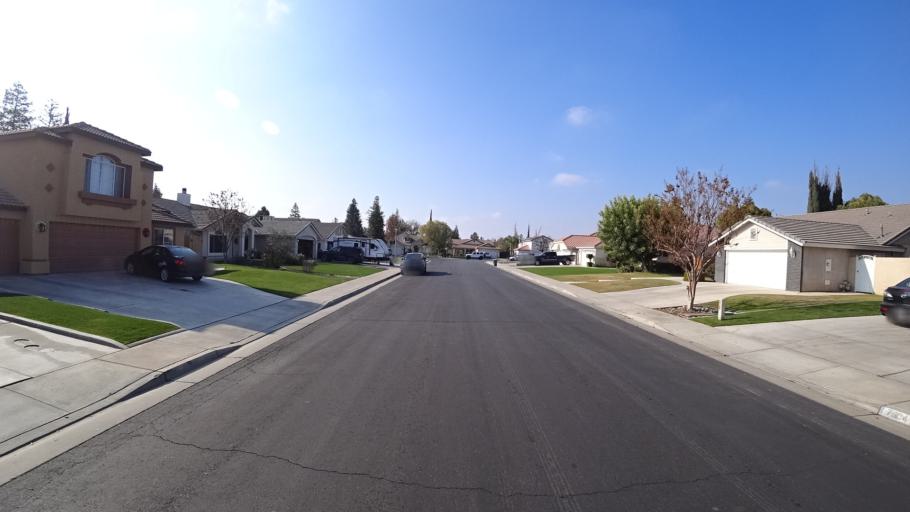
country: US
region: California
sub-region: Kern County
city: Greenacres
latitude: 35.3022
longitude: -119.0853
